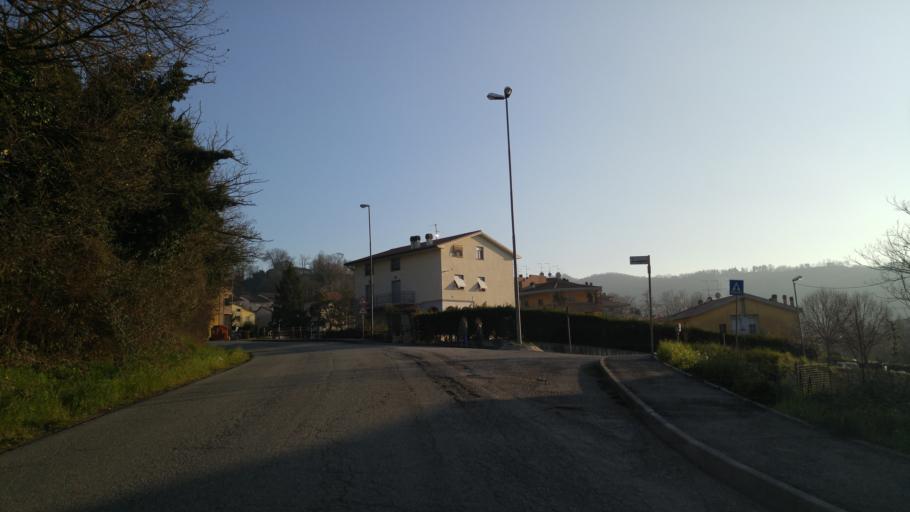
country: IT
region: The Marches
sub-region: Provincia di Pesaro e Urbino
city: Fermignano
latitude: 43.6724
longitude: 12.6482
